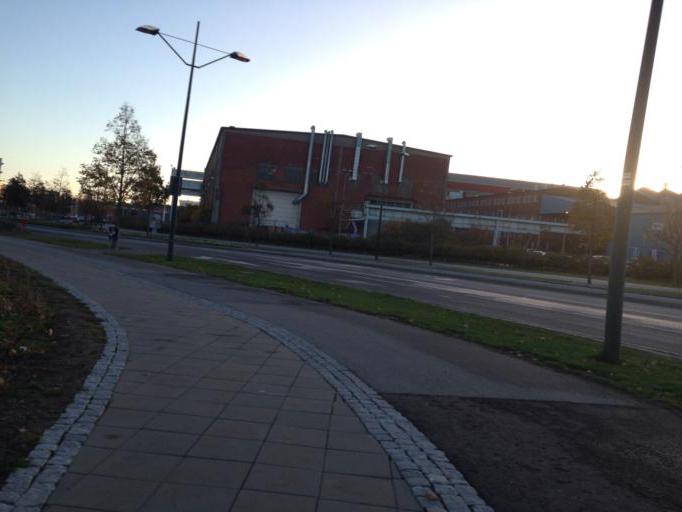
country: SE
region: Skane
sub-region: Malmo
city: Malmoe
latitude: 55.6106
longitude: 12.9820
